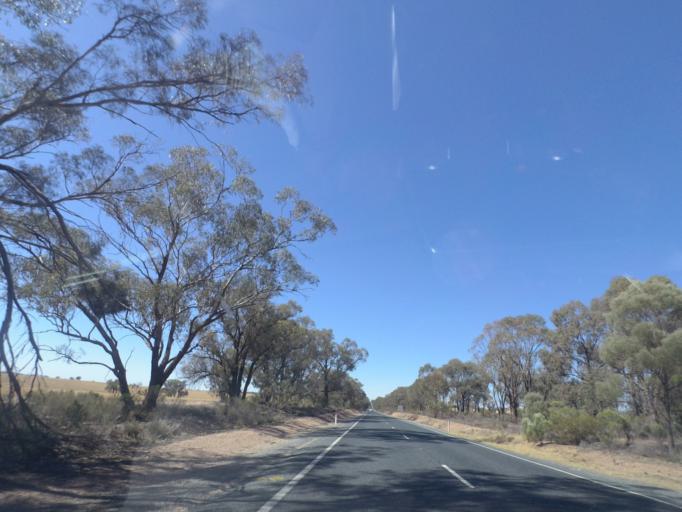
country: AU
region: New South Wales
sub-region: Bland
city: West Wyalong
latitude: -34.1436
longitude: 147.1197
